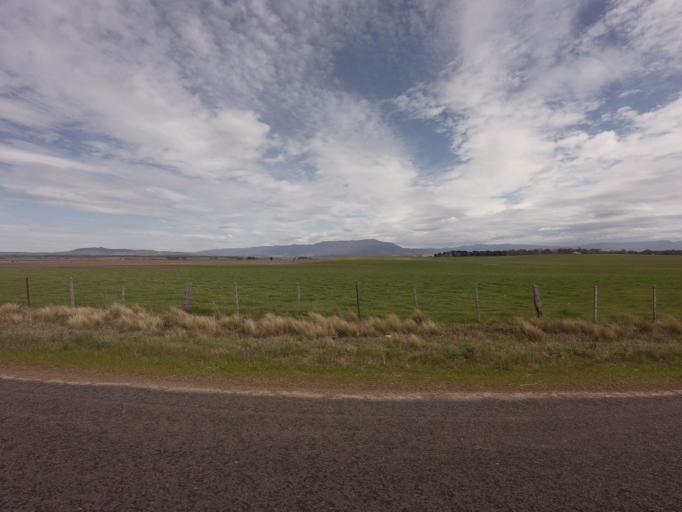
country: AU
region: Tasmania
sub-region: Northern Midlands
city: Evandale
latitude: -41.8041
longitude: 147.2723
